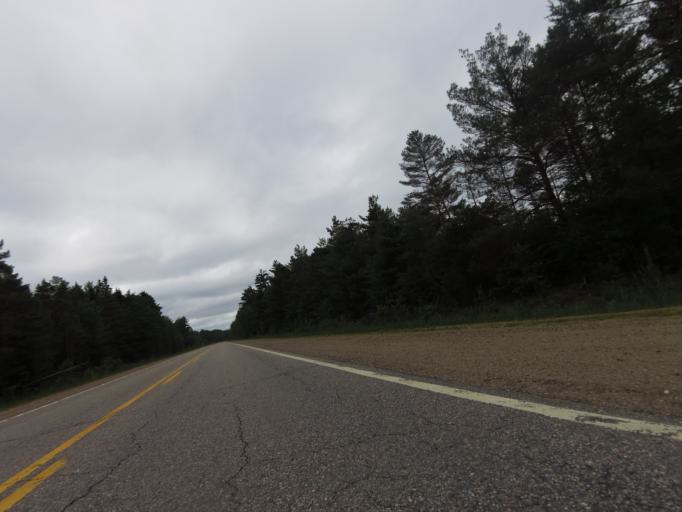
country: CA
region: Quebec
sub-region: Outaouais
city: Shawville
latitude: 45.8686
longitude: -76.4058
